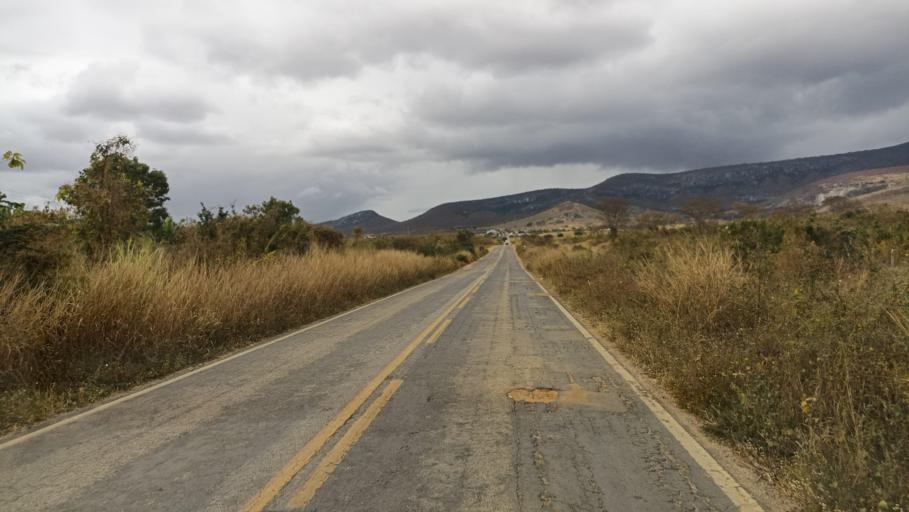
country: BR
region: Minas Gerais
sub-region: Itinga
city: Itinga
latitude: -16.6244
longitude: -41.7801
